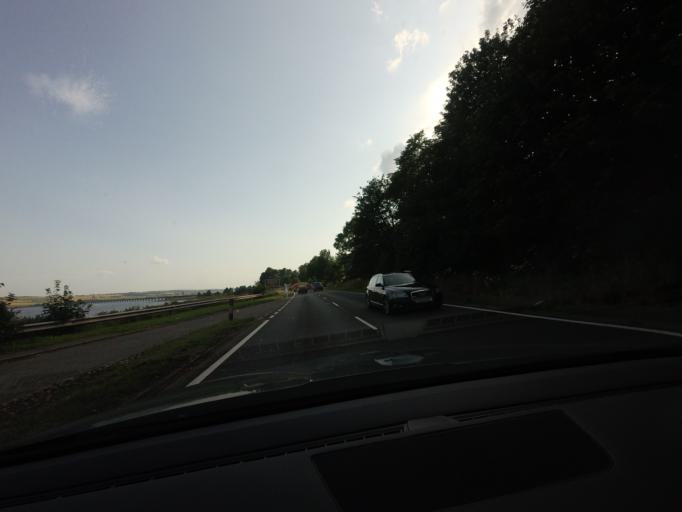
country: GB
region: Scotland
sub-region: Highland
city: Evanton
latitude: 57.6319
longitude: -4.3647
